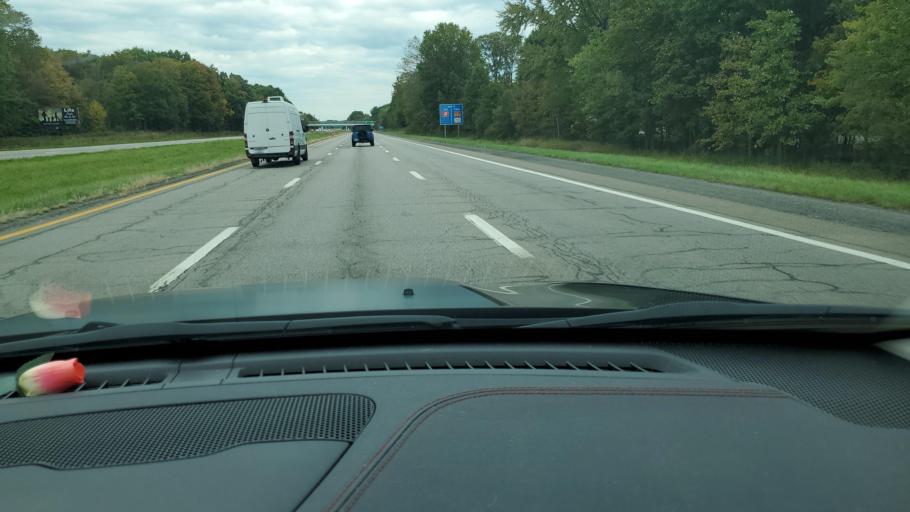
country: US
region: Ohio
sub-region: Mahoning County
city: Struthers
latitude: 41.0438
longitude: -80.6306
